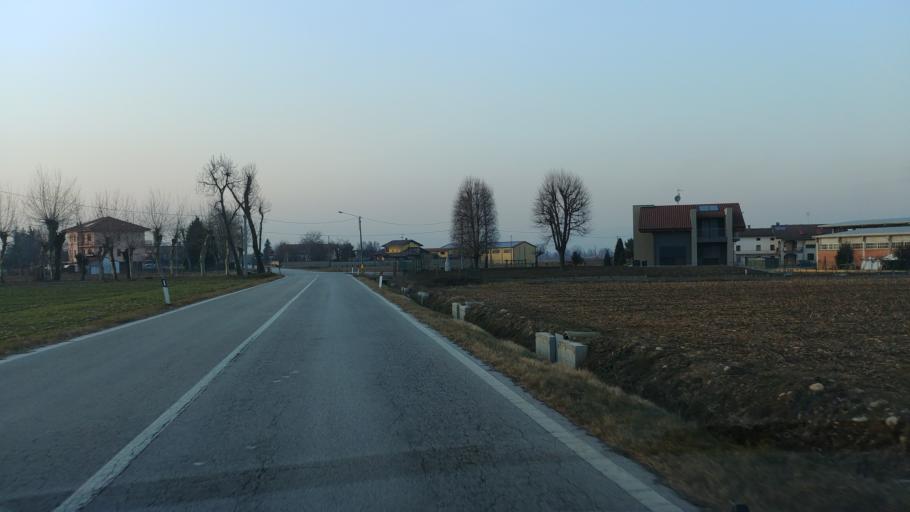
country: IT
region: Piedmont
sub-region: Provincia di Cuneo
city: Roata Rossi
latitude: 44.4229
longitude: 7.5280
